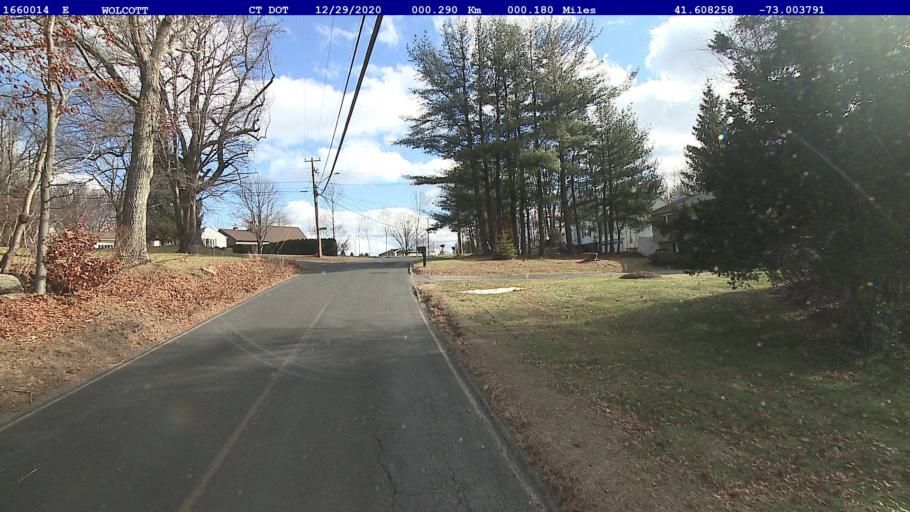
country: US
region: Connecticut
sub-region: New Haven County
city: Wolcott
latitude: 41.6082
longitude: -73.0038
